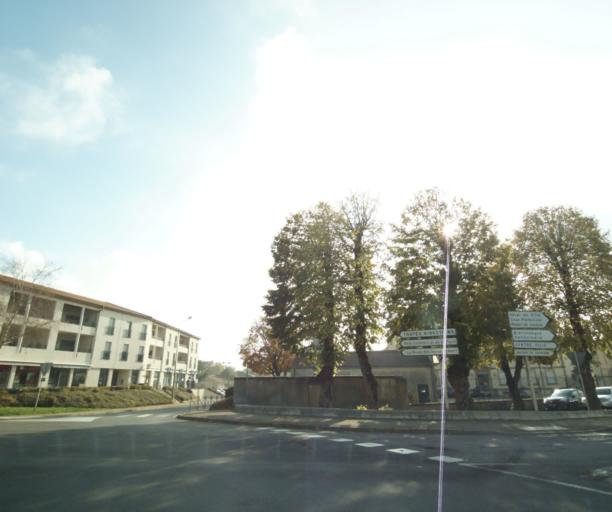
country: FR
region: Lorraine
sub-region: Departement de Meurthe-et-Moselle
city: Briey
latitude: 49.2512
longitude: 5.9386
